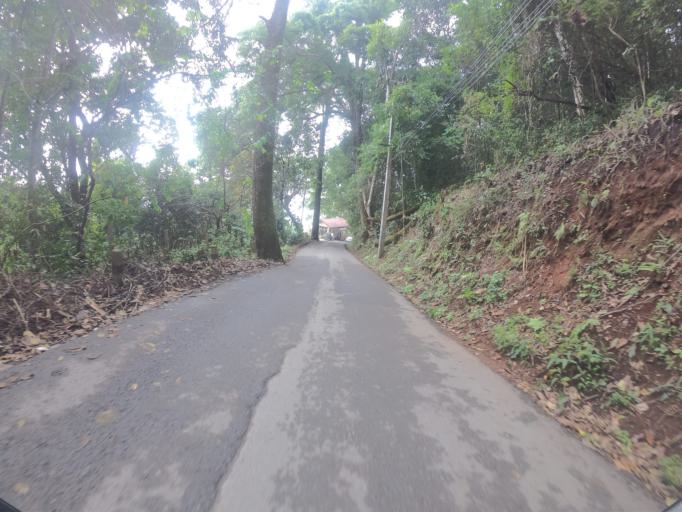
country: TH
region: Chiang Mai
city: Chiang Mai
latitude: 18.8120
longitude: 98.8855
